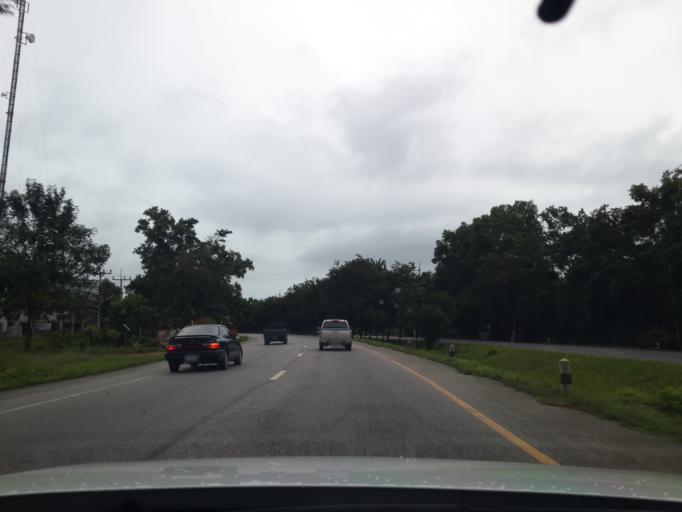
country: TH
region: Songkhla
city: Na Mom
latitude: 6.9552
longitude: 100.5591
